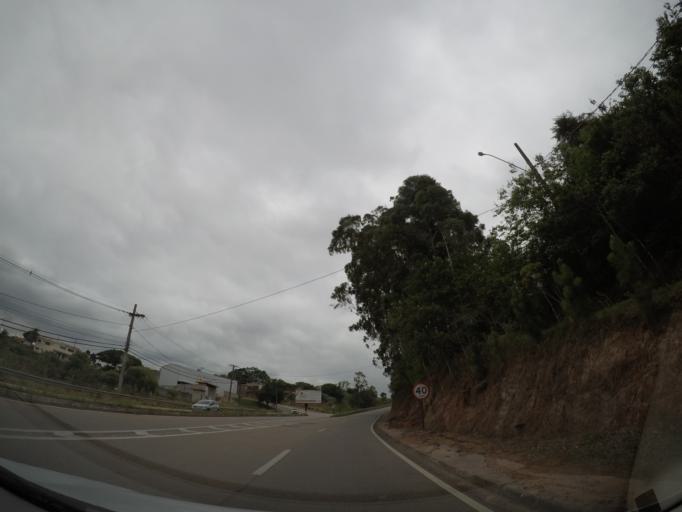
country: BR
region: Sao Paulo
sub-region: Louveira
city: Louveira
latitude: -23.1246
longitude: -46.9324
